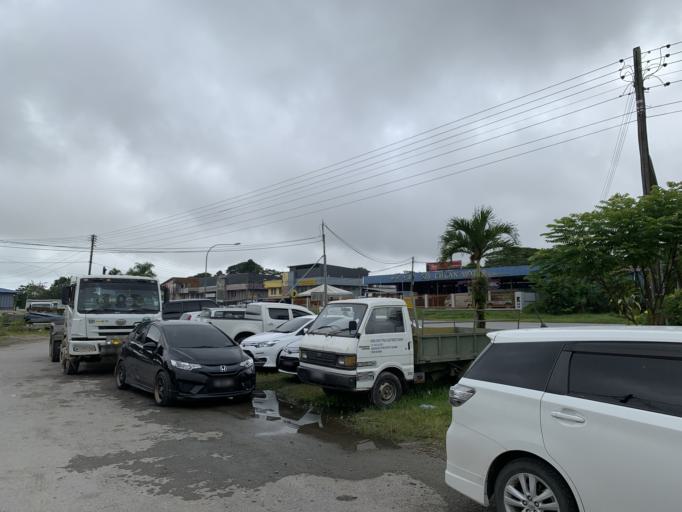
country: MY
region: Sarawak
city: Simanggang
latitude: 1.2238
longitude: 111.4671
